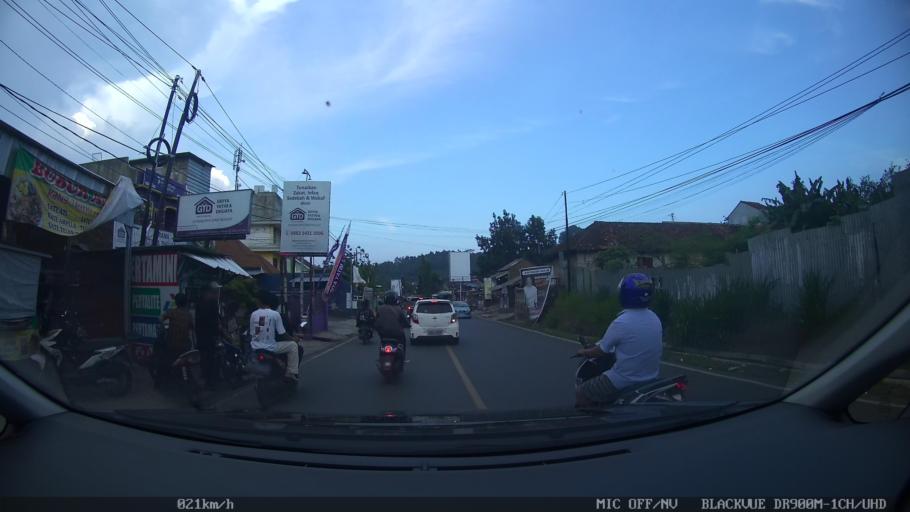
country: ID
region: Lampung
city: Kedaton
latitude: -5.3930
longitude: 105.2173
